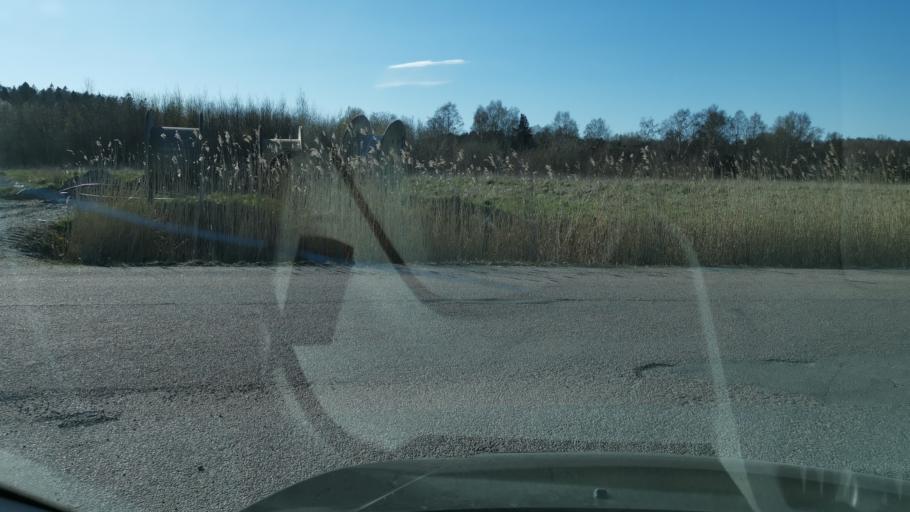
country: SE
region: Vaestra Goetaland
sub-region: Goteborg
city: Majorna
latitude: 57.7783
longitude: 11.8636
